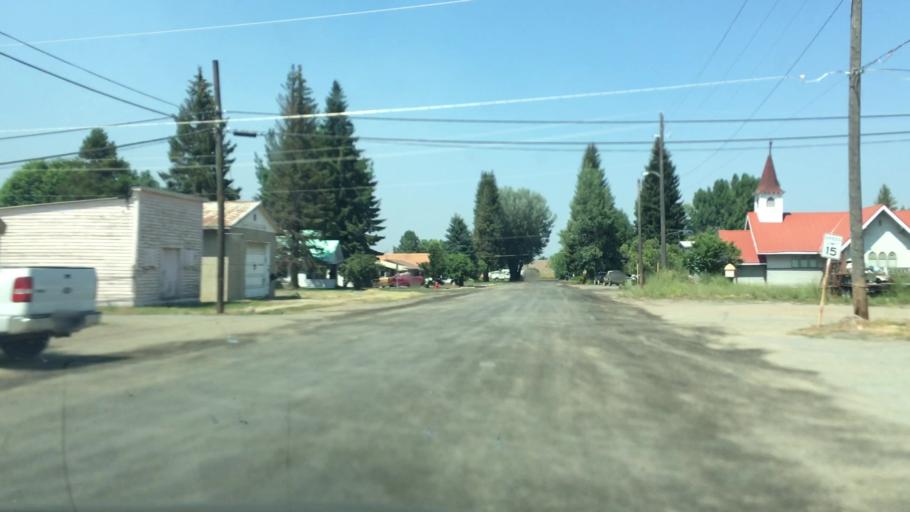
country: US
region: Idaho
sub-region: Valley County
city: McCall
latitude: 44.9713
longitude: -116.2844
